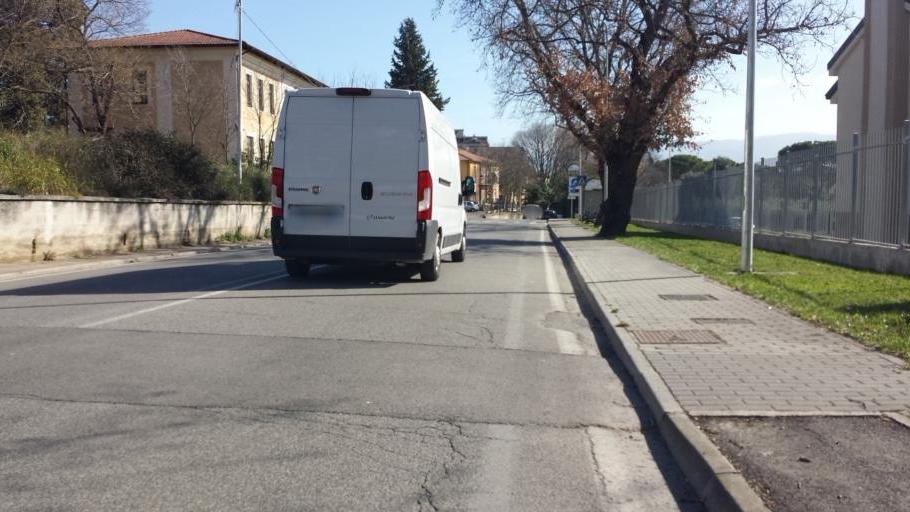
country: IT
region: Umbria
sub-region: Provincia di Terni
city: Terni
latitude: 42.5846
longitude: 12.6134
